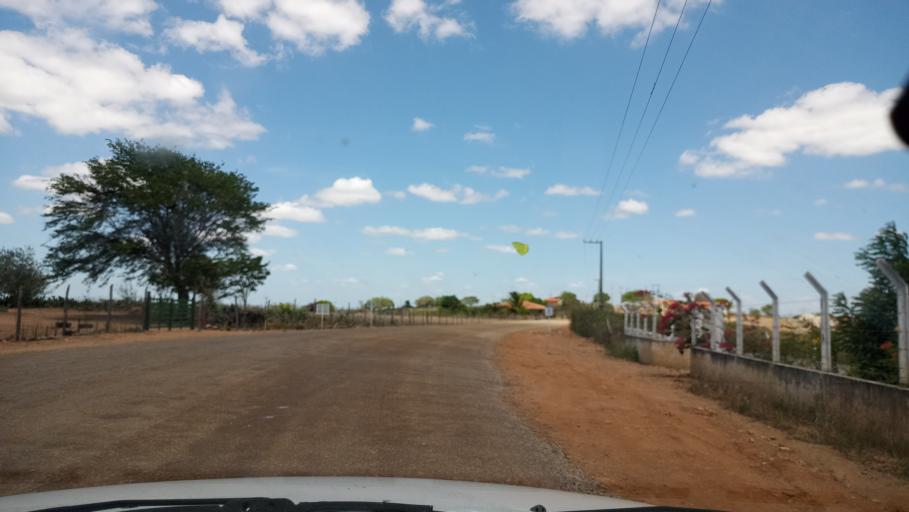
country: BR
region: Rio Grande do Norte
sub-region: Sao Paulo Do Potengi
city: Sao Paulo do Potengi
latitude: -5.7839
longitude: -35.9153
